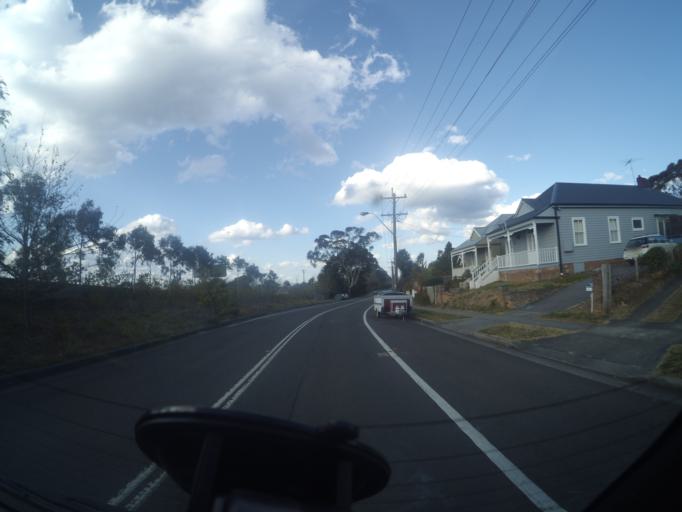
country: AU
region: New South Wales
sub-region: Blue Mountains Municipality
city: Katoomba
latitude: -33.7082
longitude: 150.3039
